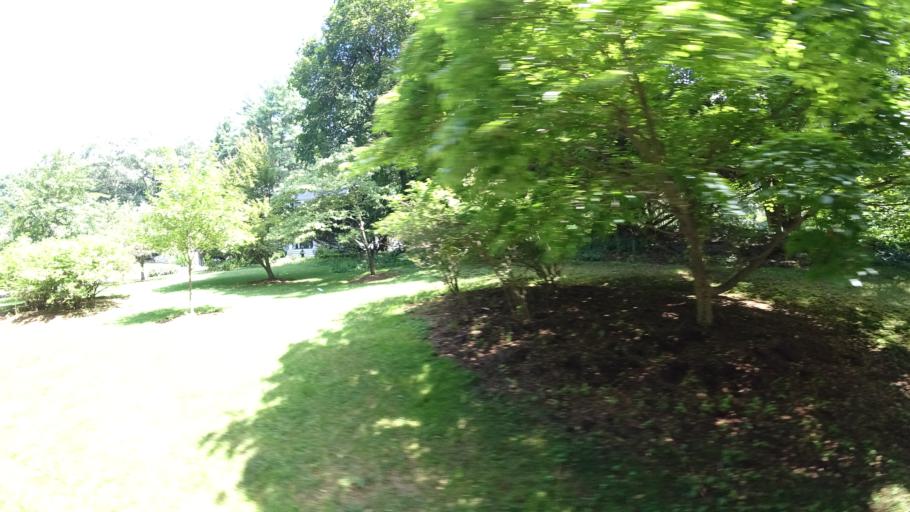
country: US
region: Massachusetts
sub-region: Norfolk County
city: Dedham
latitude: 42.2370
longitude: -71.1909
